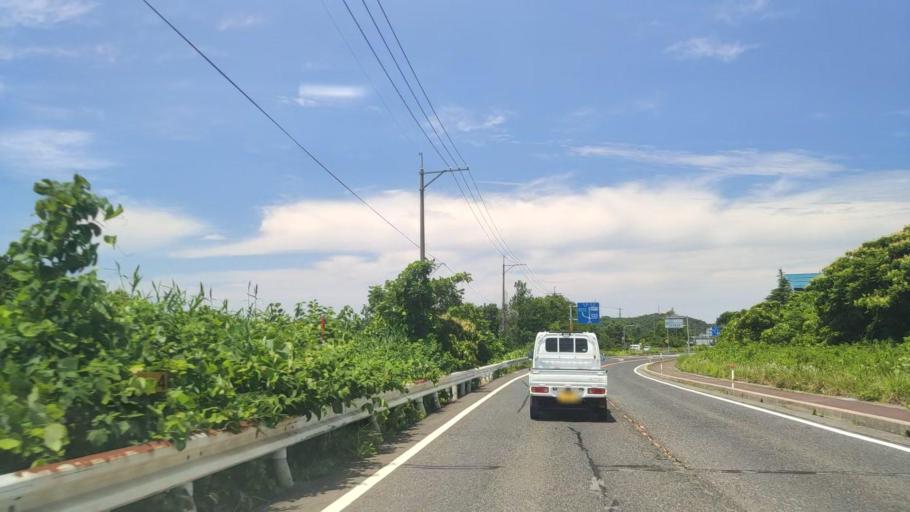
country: JP
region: Tottori
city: Tottori
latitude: 35.4398
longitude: 134.2560
